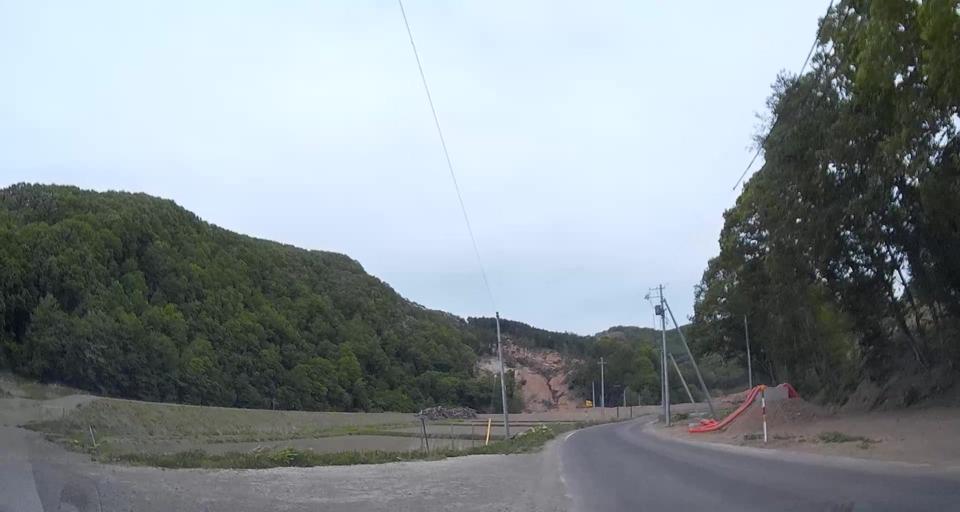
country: JP
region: Hokkaido
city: Chitose
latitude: 42.7615
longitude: 141.9794
